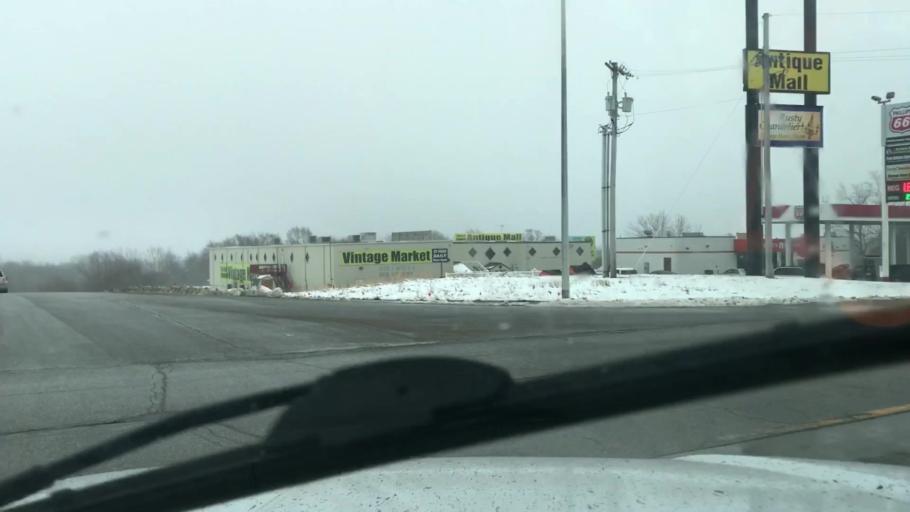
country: US
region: Missouri
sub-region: Andrew County
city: Country Club Village
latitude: 39.8572
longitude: -94.8110
